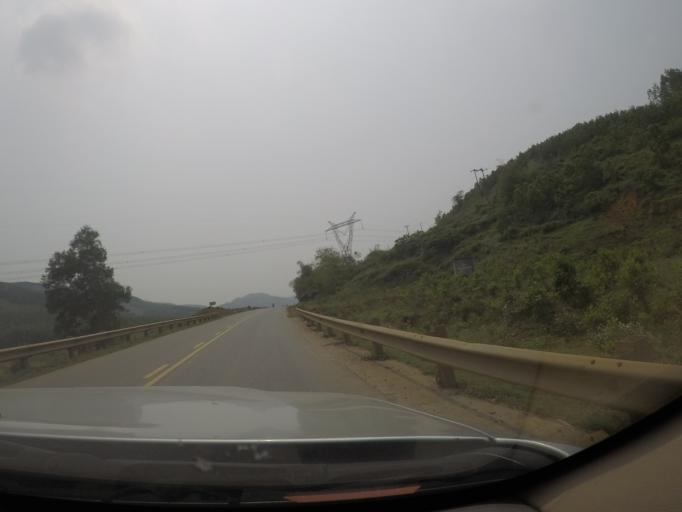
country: VN
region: Thanh Hoa
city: Thi Tran Cam Thuy
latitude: 20.1792
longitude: 105.4792
